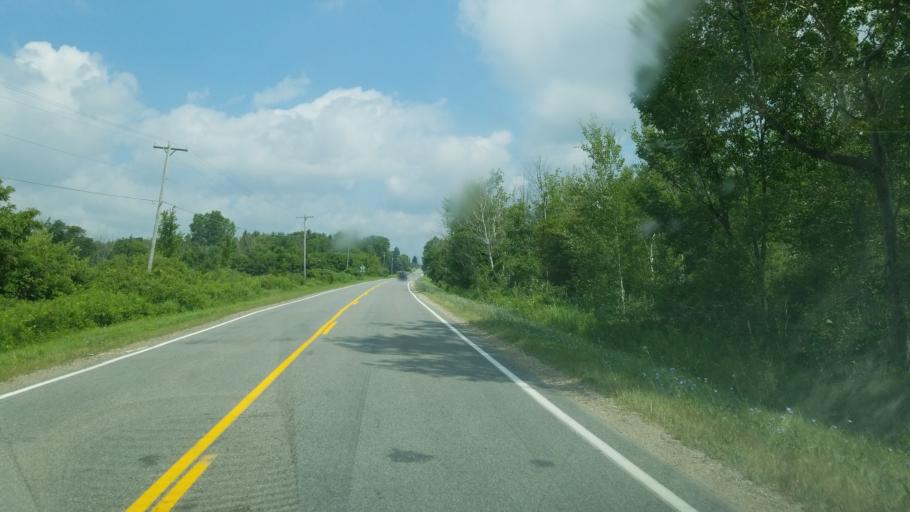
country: US
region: Michigan
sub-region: Kent County
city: Kent City
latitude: 43.2055
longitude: -85.7112
